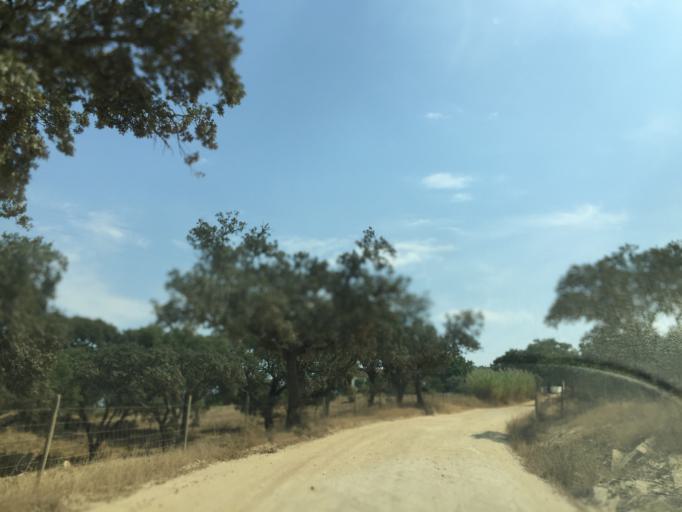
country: PT
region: Setubal
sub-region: Grandola
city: Grandola
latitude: 38.0118
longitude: -8.4847
